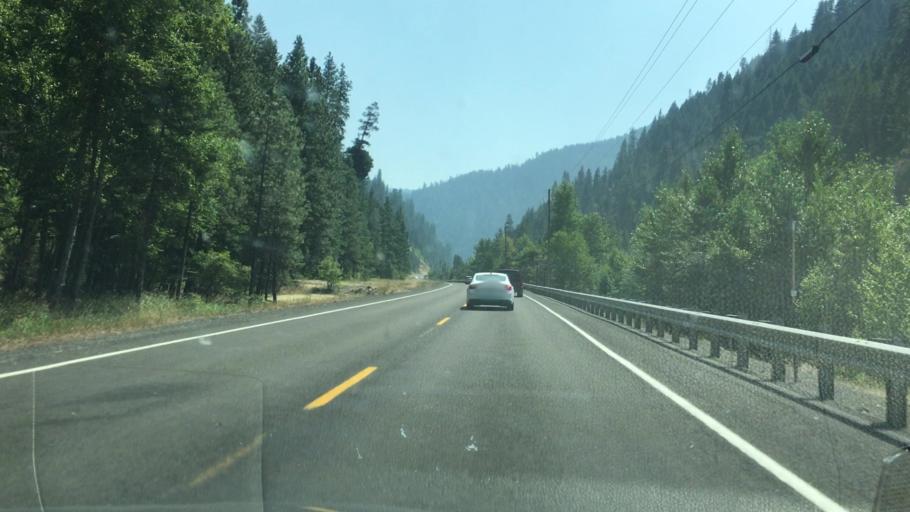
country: US
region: Idaho
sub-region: Valley County
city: McCall
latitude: 45.1648
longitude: -116.3015
